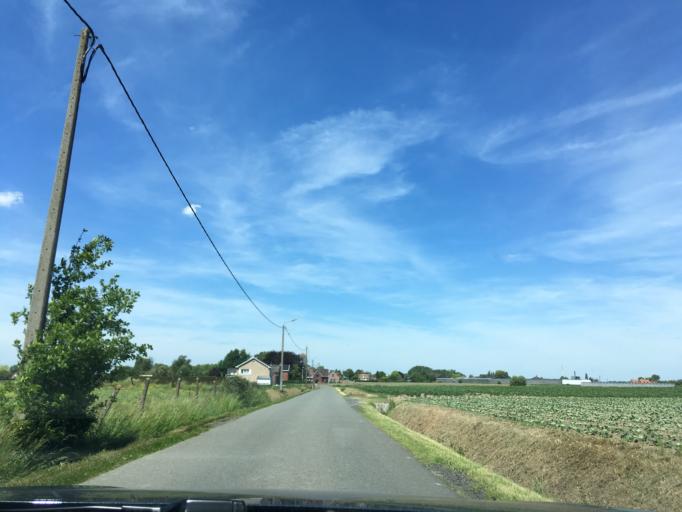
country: BE
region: Flanders
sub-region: Provincie West-Vlaanderen
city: Hooglede
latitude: 51.0007
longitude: 3.0981
